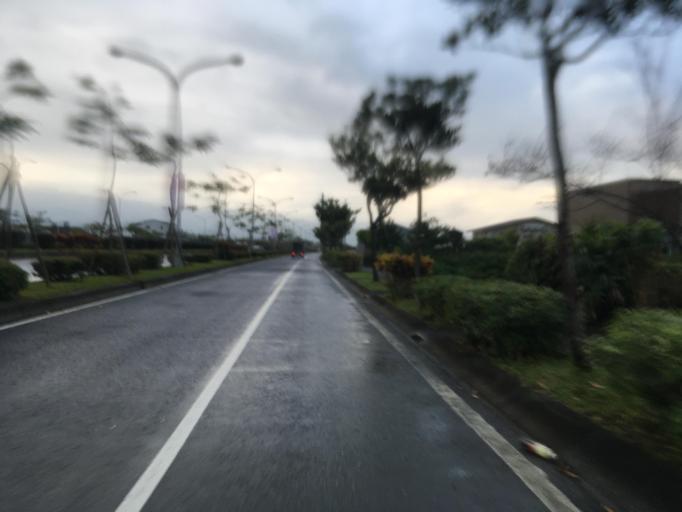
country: TW
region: Taiwan
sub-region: Yilan
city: Yilan
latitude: 24.7276
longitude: 121.7722
